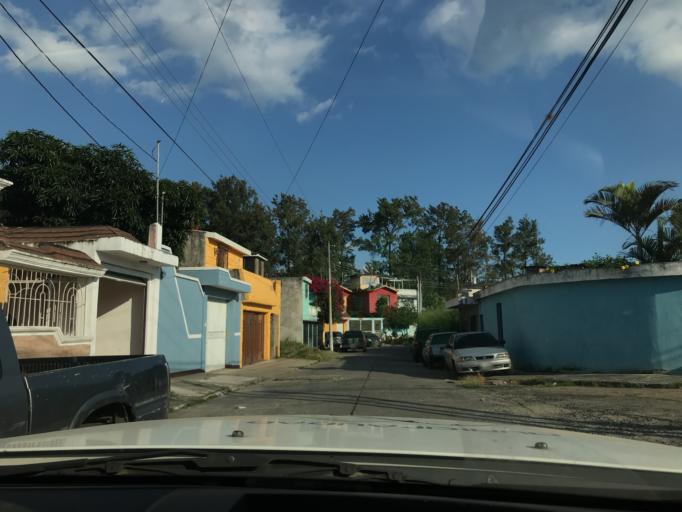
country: GT
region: Guatemala
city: Petapa
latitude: 14.4926
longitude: -90.5467
